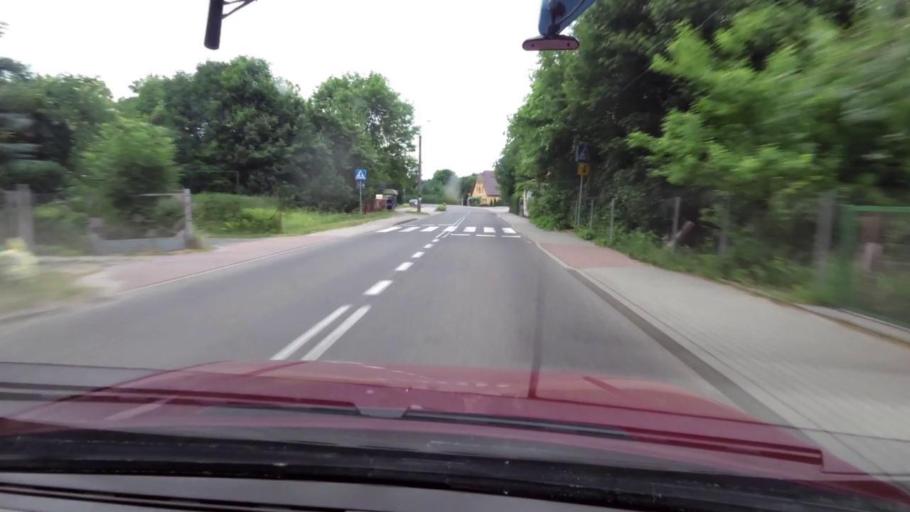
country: PL
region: West Pomeranian Voivodeship
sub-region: Powiat koszalinski
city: Sianow
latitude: 54.1809
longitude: 16.3816
